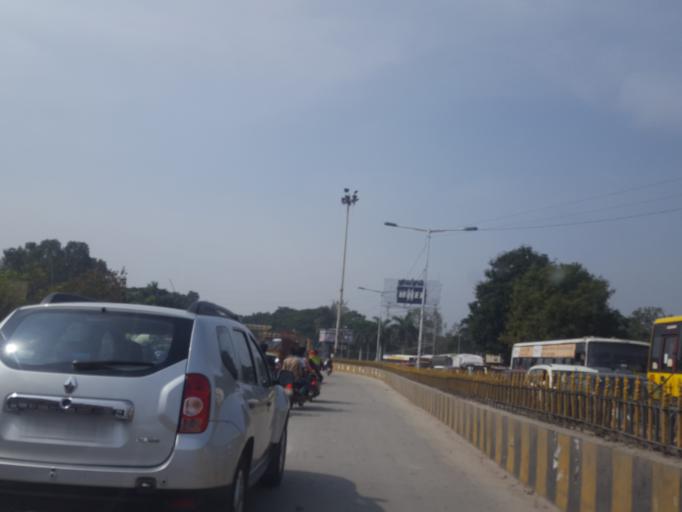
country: IN
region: Telangana
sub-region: Medak
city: Serilingampalle
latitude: 17.4950
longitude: 78.3168
